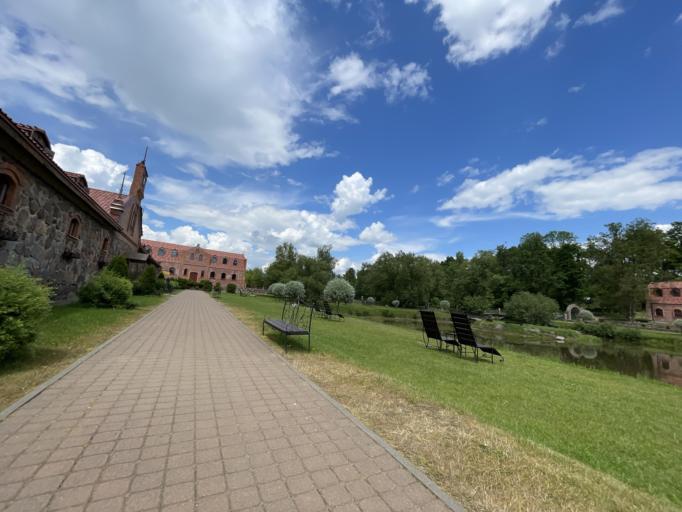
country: BY
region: Minsk
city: Ivyanyets
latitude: 53.7418
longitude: 26.8752
